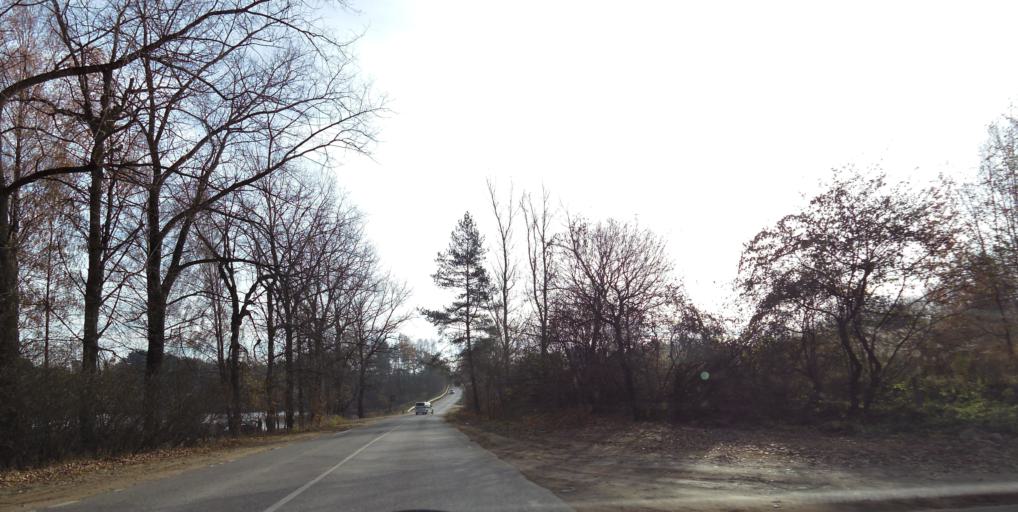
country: LT
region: Vilnius County
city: Justiniskes
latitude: 54.7138
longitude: 25.1984
